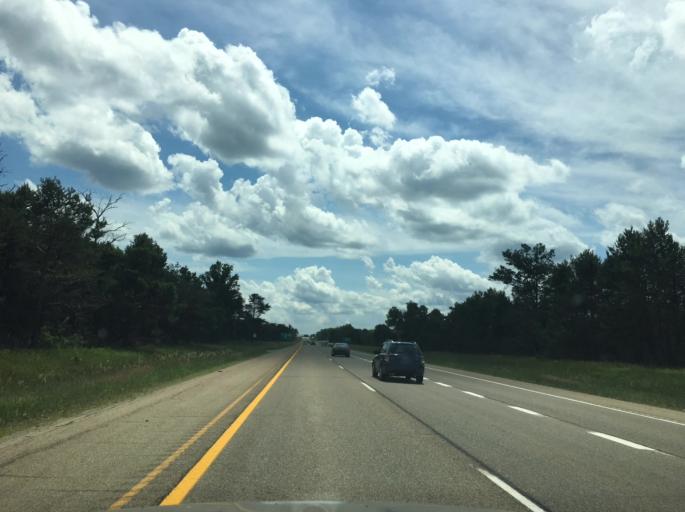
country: US
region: Michigan
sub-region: Crawford County
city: Grayling
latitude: 44.5909
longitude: -84.7096
